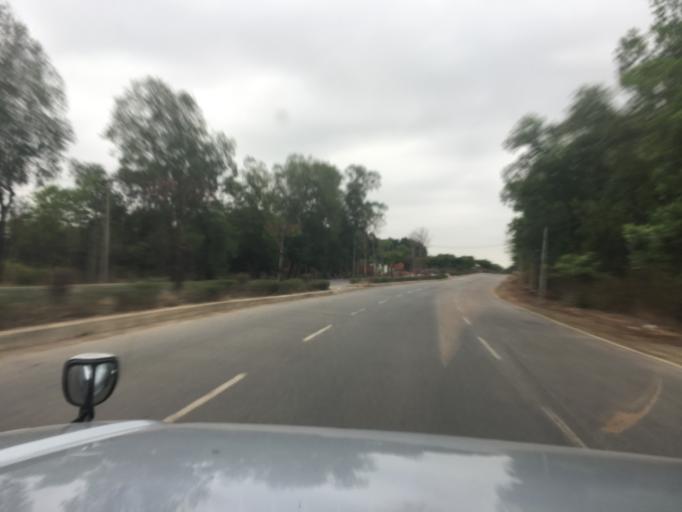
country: MM
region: Bago
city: Thanatpin
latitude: 17.2126
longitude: 96.4183
